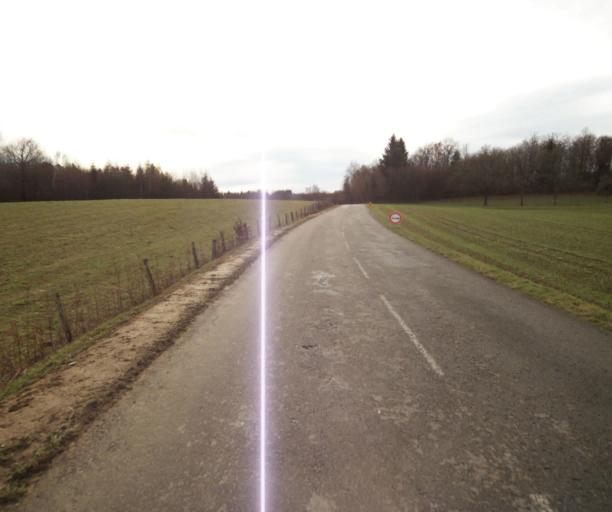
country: FR
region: Limousin
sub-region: Departement de la Correze
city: Chameyrat
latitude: 45.2519
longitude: 1.7011
